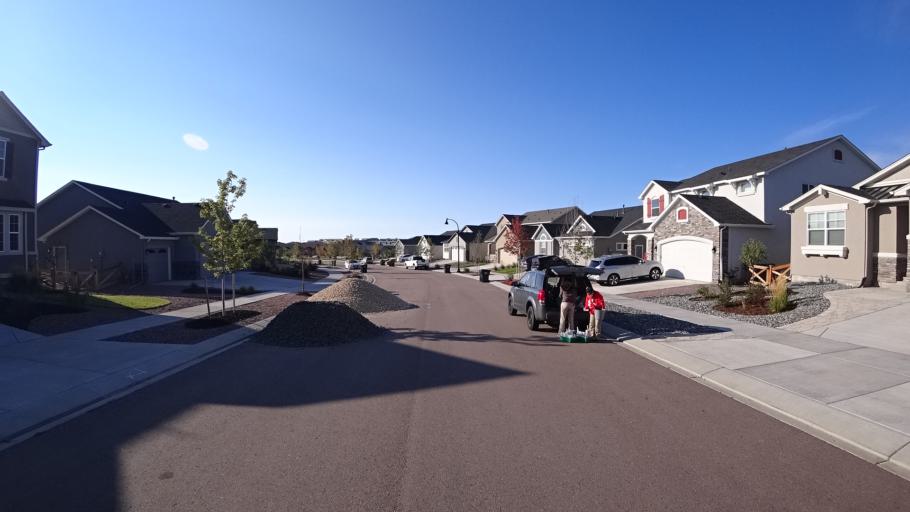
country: US
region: Colorado
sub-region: El Paso County
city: Black Forest
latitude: 38.9363
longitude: -104.6607
